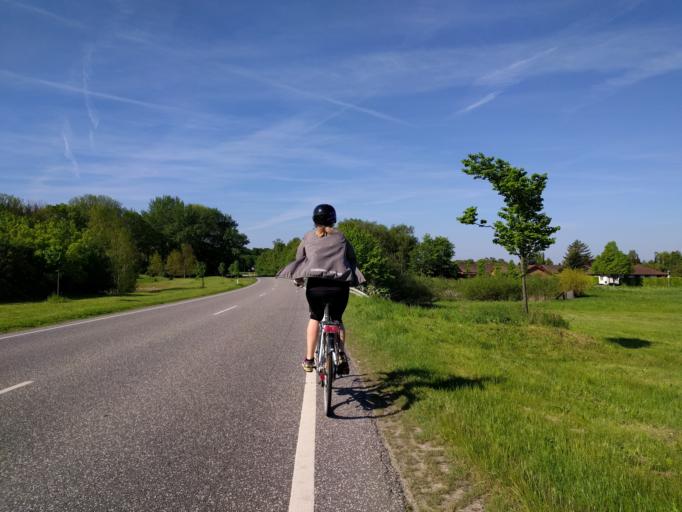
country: DK
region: Zealand
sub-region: Guldborgsund Kommune
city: Nykobing Falster
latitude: 54.7560
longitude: 11.9084
